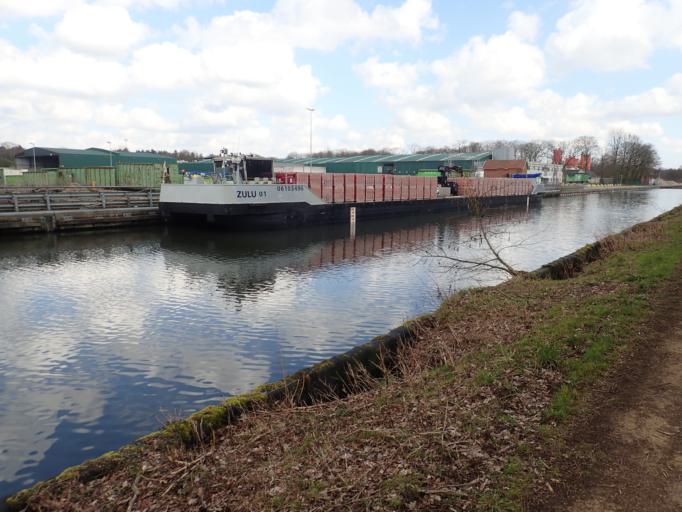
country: BE
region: Flanders
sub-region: Provincie Antwerpen
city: Vosselaar
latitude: 51.3303
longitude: 4.8865
